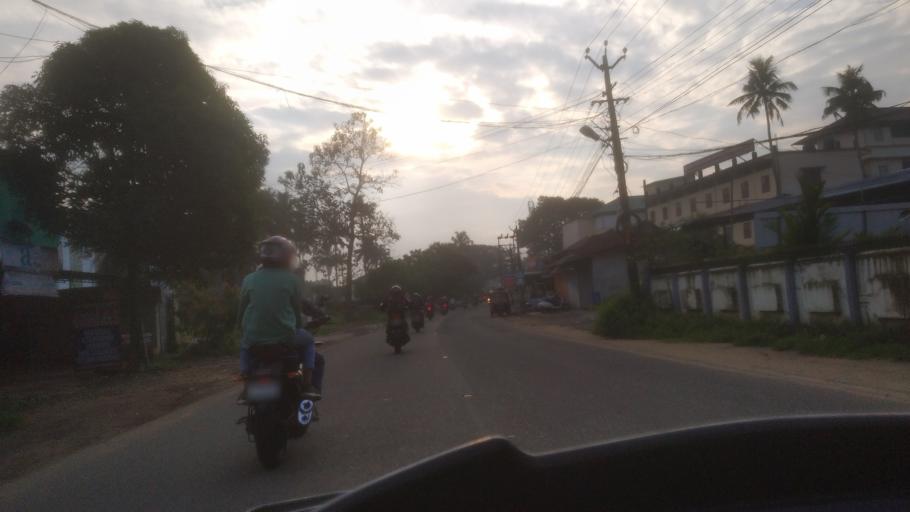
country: IN
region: Kerala
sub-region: Ernakulam
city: Perumpavur
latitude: 10.1185
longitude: 76.4413
